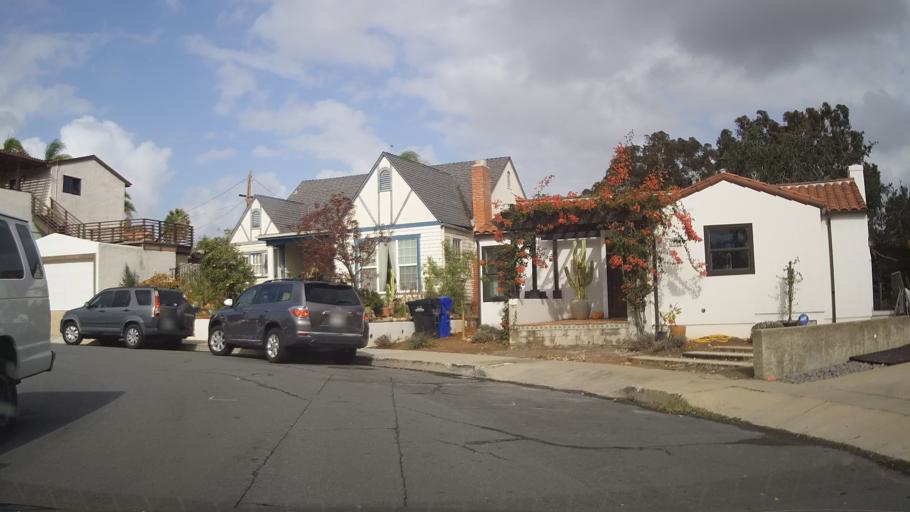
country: US
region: California
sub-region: San Diego County
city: San Diego
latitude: 32.7347
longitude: -117.1215
